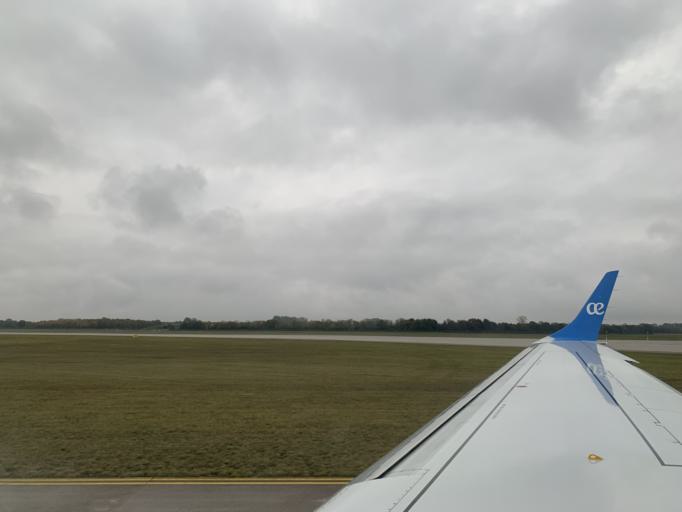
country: DE
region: Bavaria
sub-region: Upper Bavaria
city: Hallbergmoos
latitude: 48.3448
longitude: 11.7857
